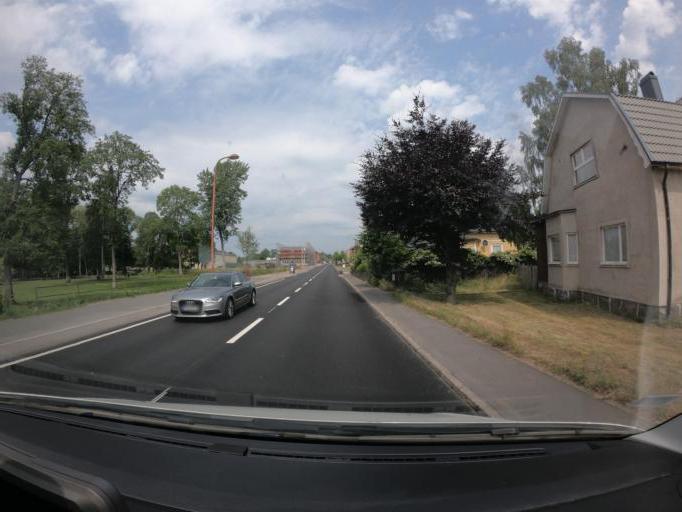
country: SE
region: Skane
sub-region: Hassleholms Kommun
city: Bjarnum
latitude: 56.2880
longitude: 13.7121
